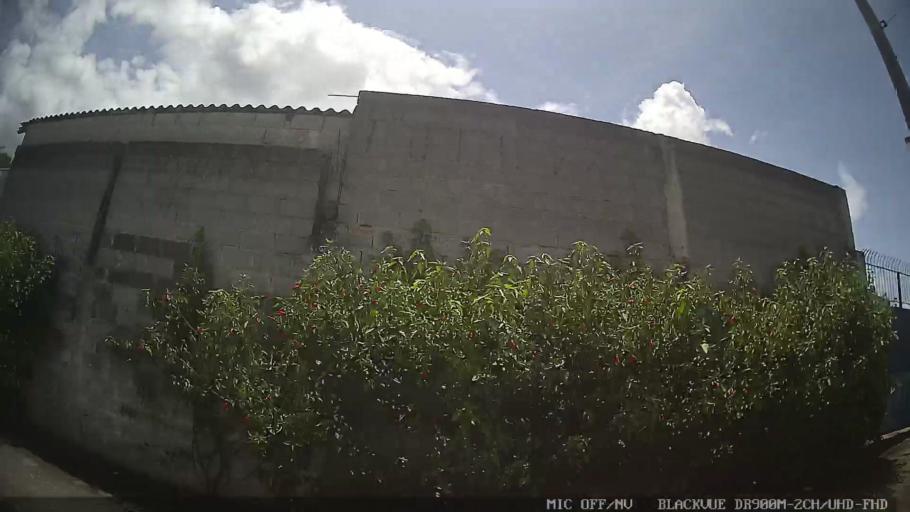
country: BR
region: Sao Paulo
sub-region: Mogi das Cruzes
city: Mogi das Cruzes
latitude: -23.5427
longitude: -46.2026
